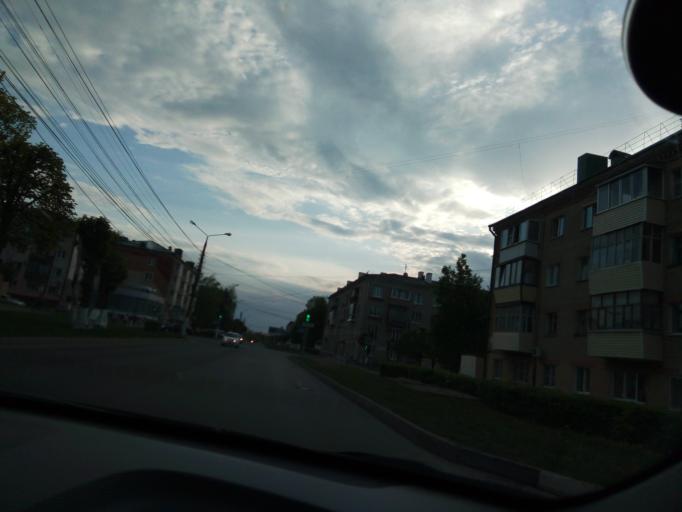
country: RU
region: Chuvashia
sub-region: Cheboksarskiy Rayon
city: Cheboksary
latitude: 56.1194
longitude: 47.2617
